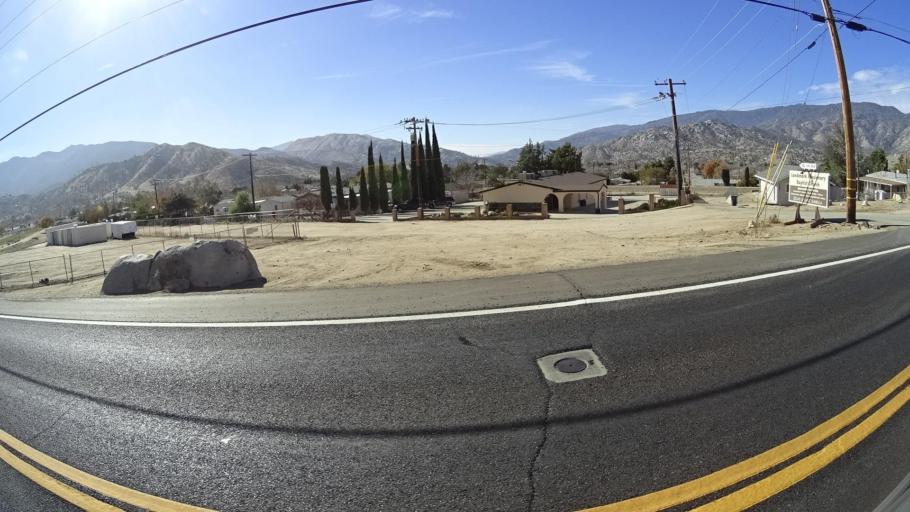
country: US
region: California
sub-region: Kern County
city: Lake Isabella
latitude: 35.6133
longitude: -118.4664
